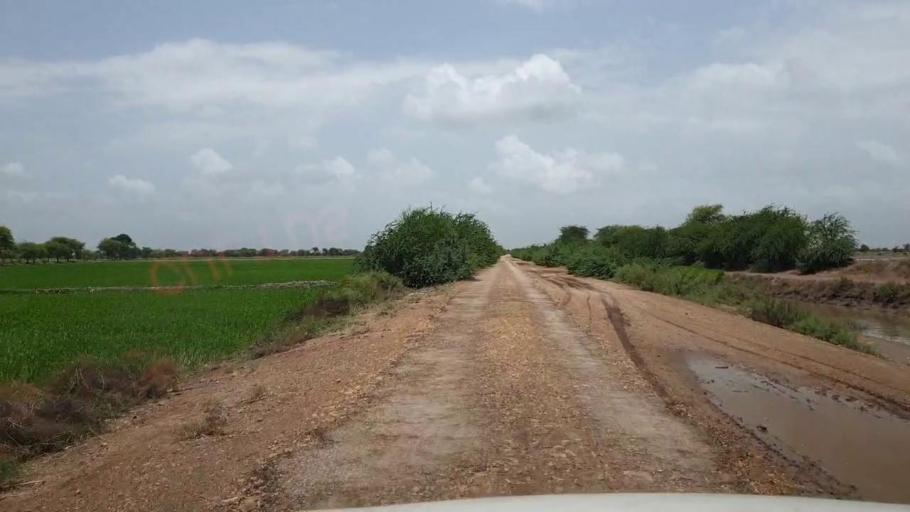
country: PK
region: Sindh
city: Kario
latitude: 24.7166
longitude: 68.5824
